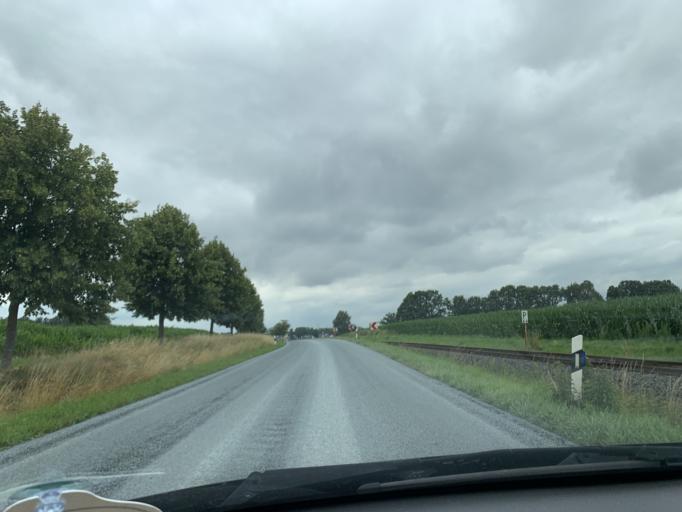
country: DE
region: North Rhine-Westphalia
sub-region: Regierungsbezirk Munster
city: Wadersloh
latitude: 51.7014
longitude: 8.2675
